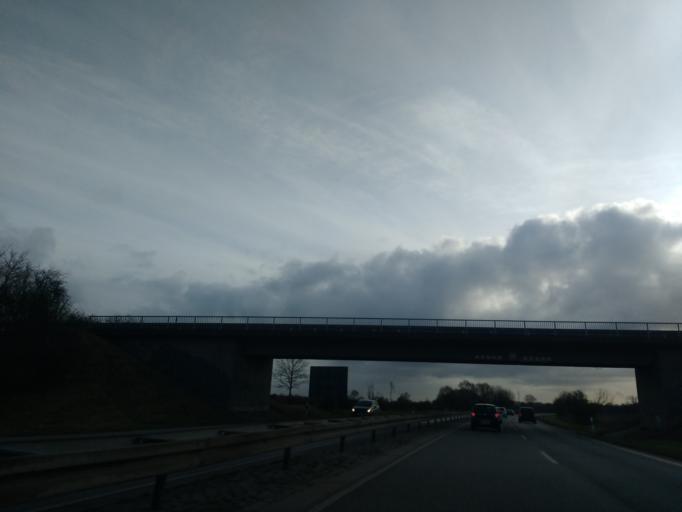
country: DE
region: Schleswig-Holstein
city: Krogaspe
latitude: 54.1181
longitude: 9.9602
